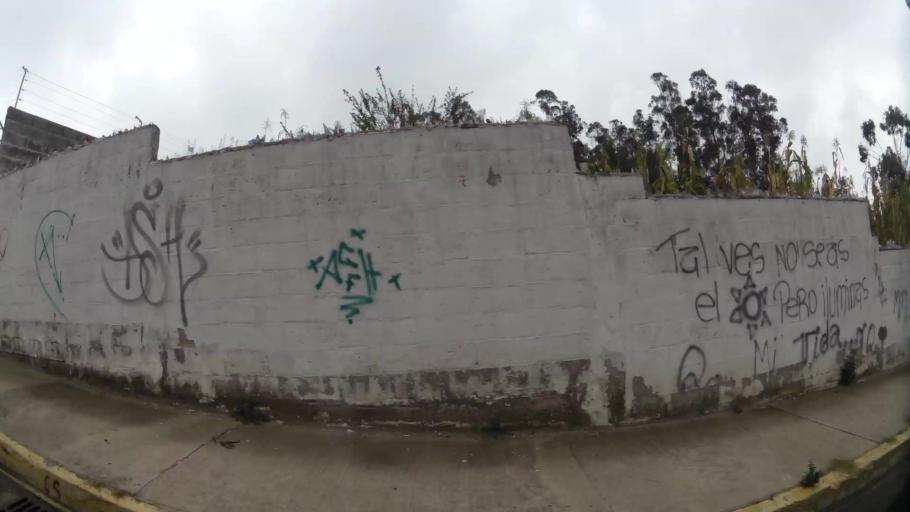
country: EC
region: Pichincha
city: Quito
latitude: -0.2644
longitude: -78.4775
